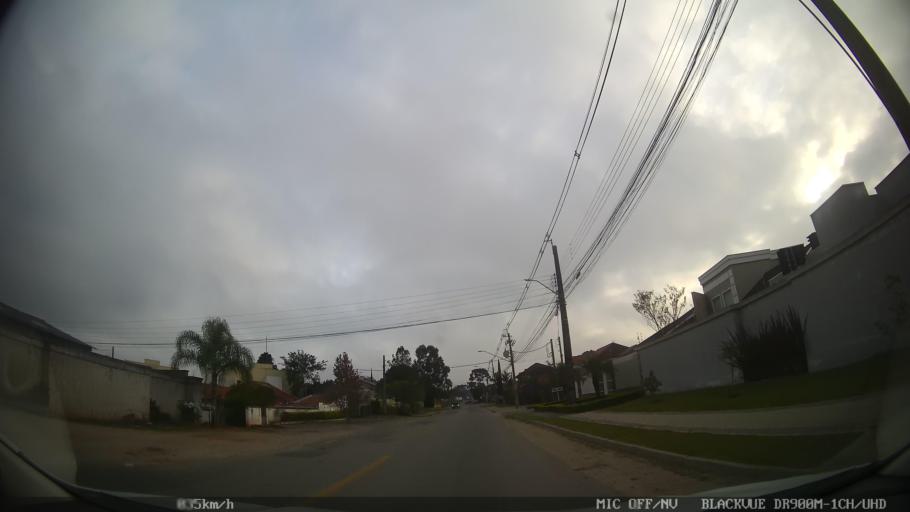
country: BR
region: Parana
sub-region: Almirante Tamandare
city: Almirante Tamandare
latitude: -25.3857
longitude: -49.3384
